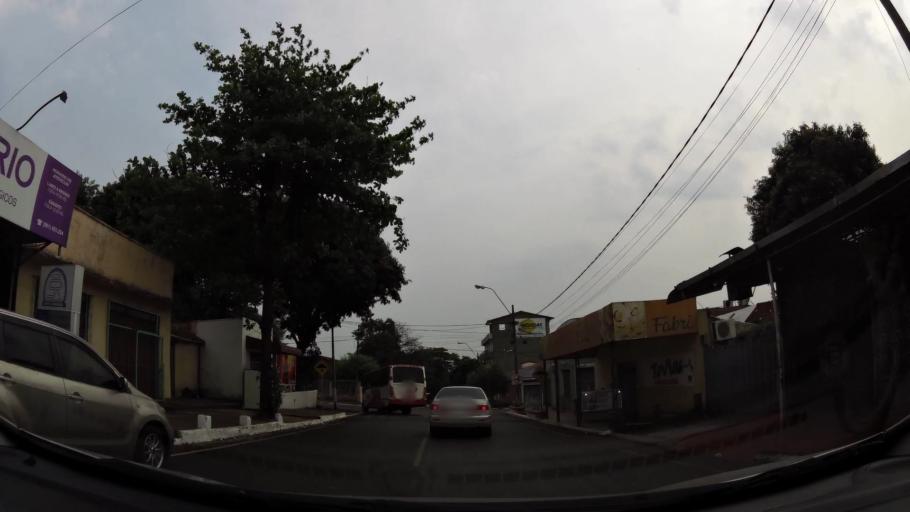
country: BR
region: Parana
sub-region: Foz Do Iguacu
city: Foz do Iguacu
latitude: -25.5569
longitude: -54.6053
